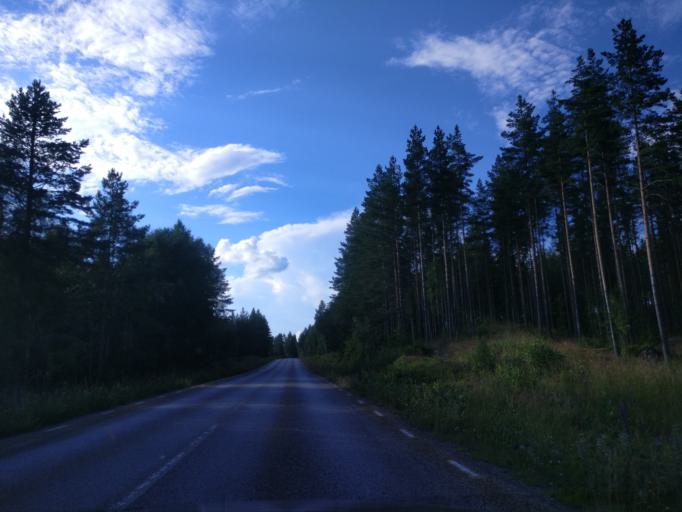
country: SE
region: Dalarna
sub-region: Ludvika Kommun
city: Ludvika
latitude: 60.2895
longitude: 15.1370
